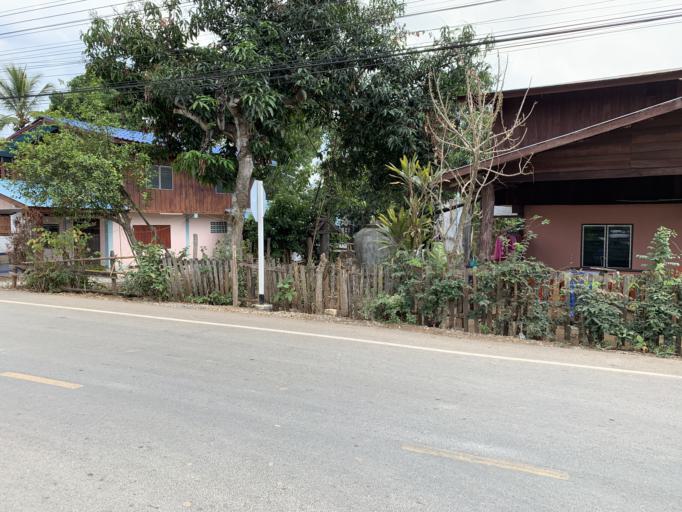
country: TH
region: Nan
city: Wiang Sa
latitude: 18.6229
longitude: 100.8330
